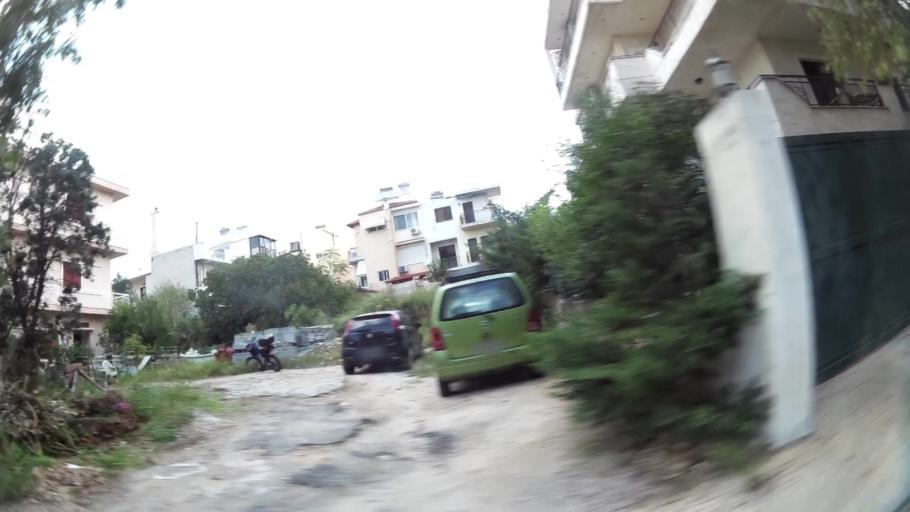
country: GR
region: Attica
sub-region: Nomarchia Athinas
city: Melissia
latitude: 38.0462
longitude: 23.8346
